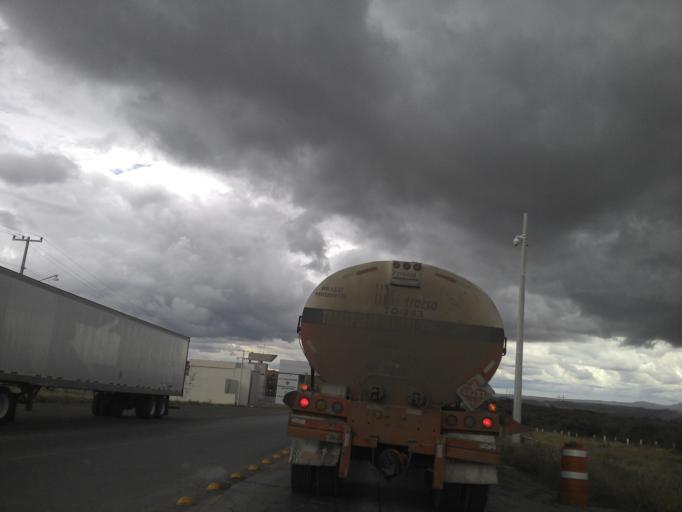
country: MX
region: Zacatecas
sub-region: Rio Grande
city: Los Condes
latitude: 23.8720
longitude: -103.0860
